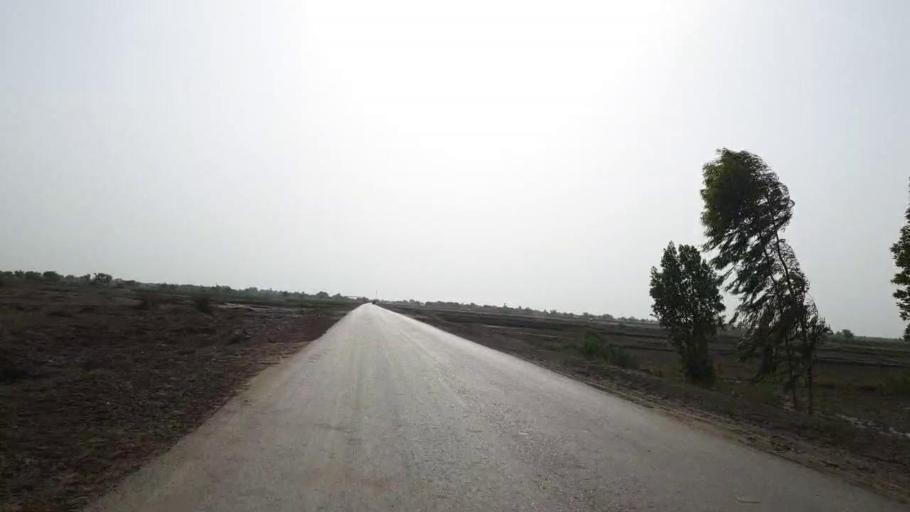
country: PK
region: Sindh
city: Nawabshah
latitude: 26.2627
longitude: 68.4955
